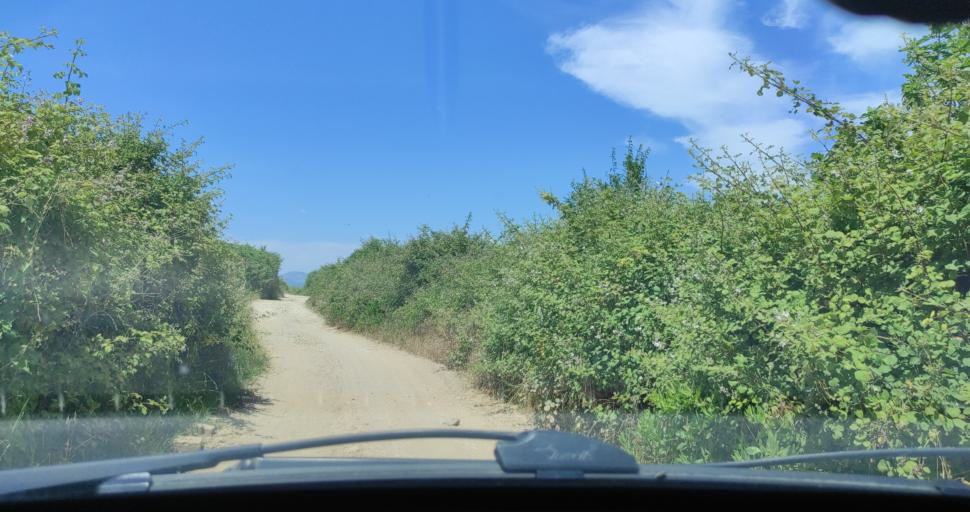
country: AL
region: Shkoder
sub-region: Rrethi i Shkodres
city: Velipoje
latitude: 41.8823
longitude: 19.3924
